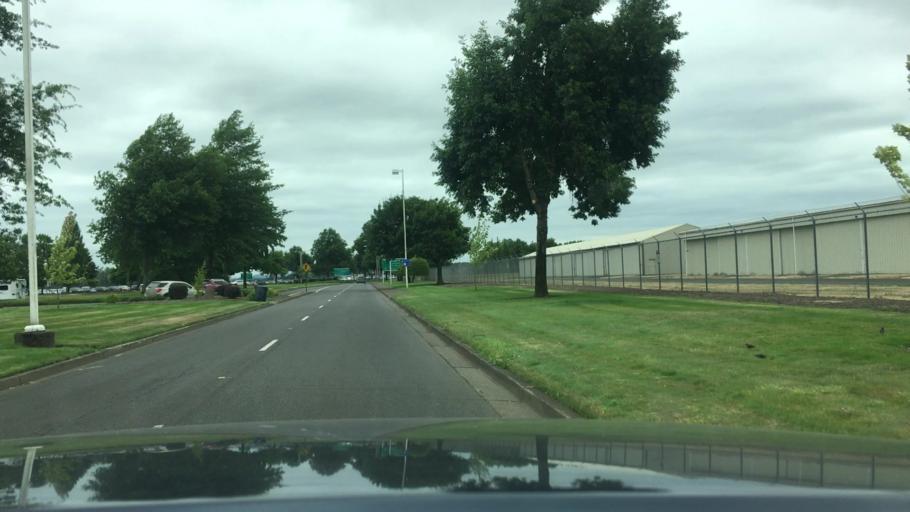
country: US
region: Oregon
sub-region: Lane County
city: Junction City
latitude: 44.1173
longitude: -123.2113
